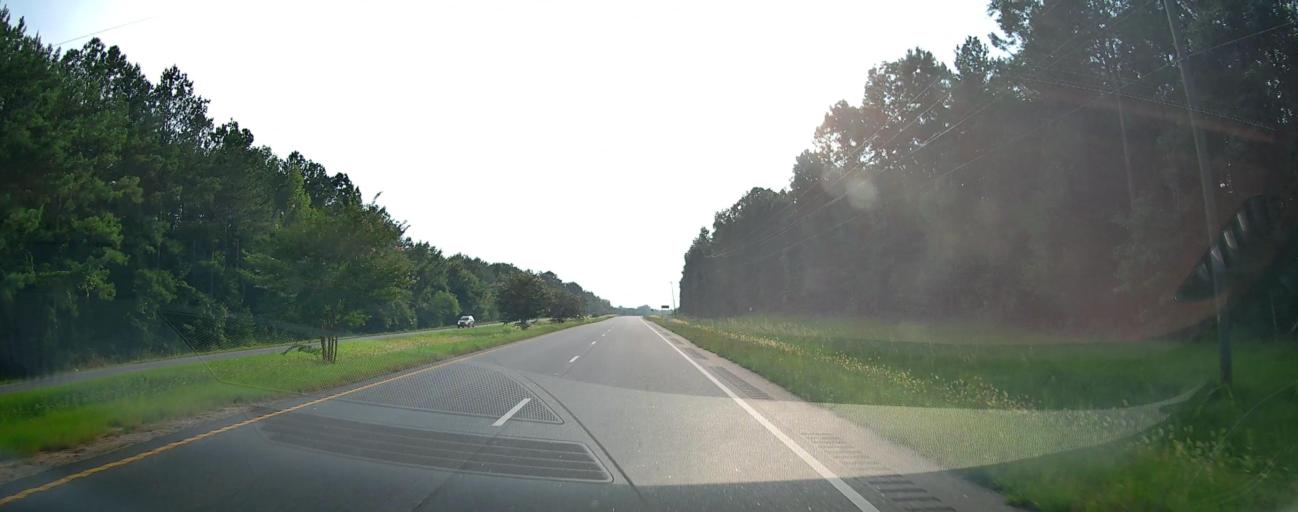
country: US
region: Georgia
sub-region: Talbot County
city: Talbotton
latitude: 32.5459
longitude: -84.7180
